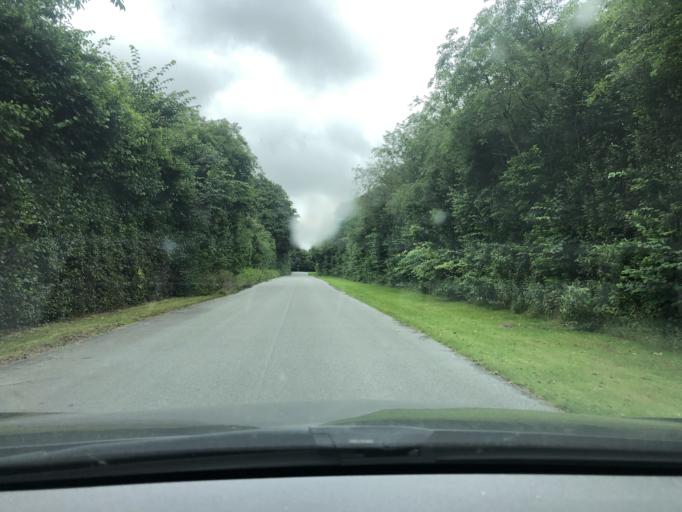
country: DK
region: South Denmark
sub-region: Varde Kommune
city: Oksbol
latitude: 55.8343
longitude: 8.2715
